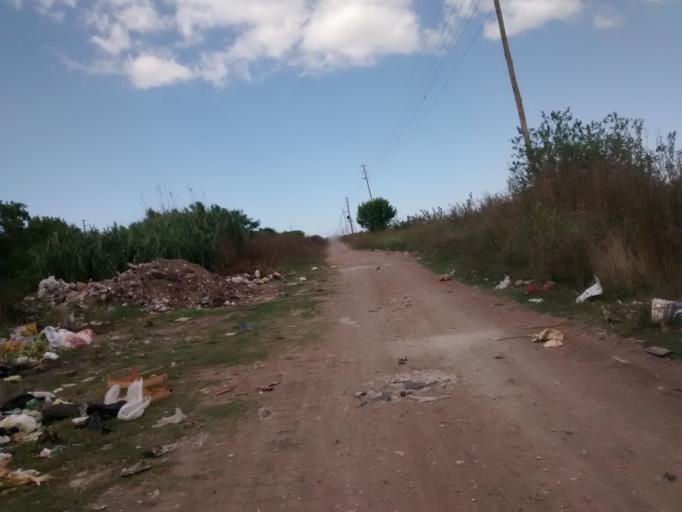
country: AR
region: Buenos Aires
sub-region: Partido de La Plata
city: La Plata
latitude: -34.9714
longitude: -57.9398
